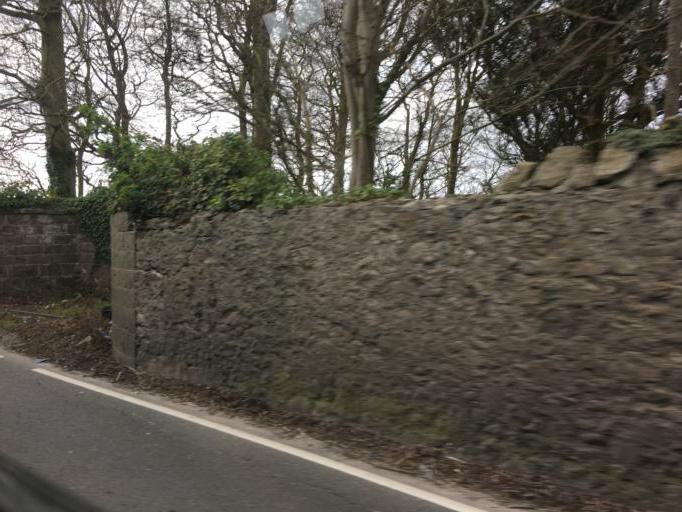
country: GB
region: Wales
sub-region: Gwynedd
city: Caernarfon
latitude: 53.1541
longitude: -4.2595
